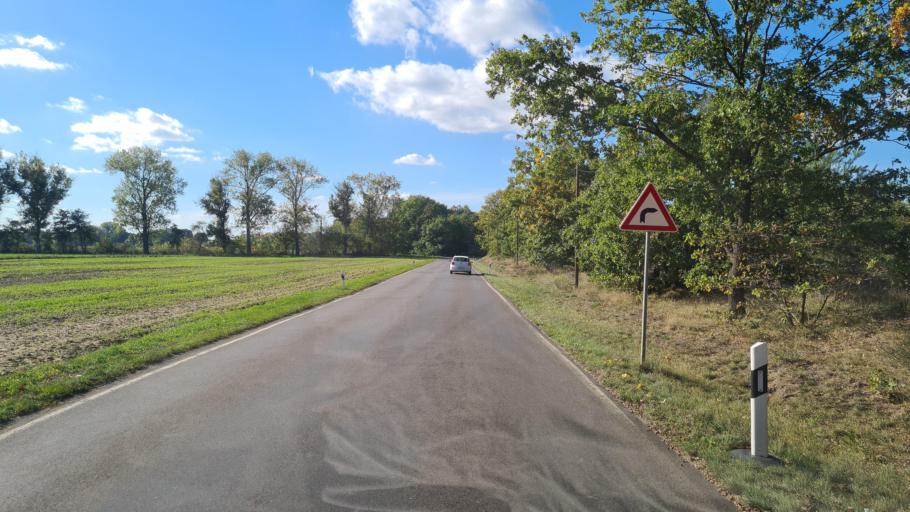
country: DE
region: Brandenburg
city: Kolkwitz
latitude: 51.7635
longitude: 14.2714
